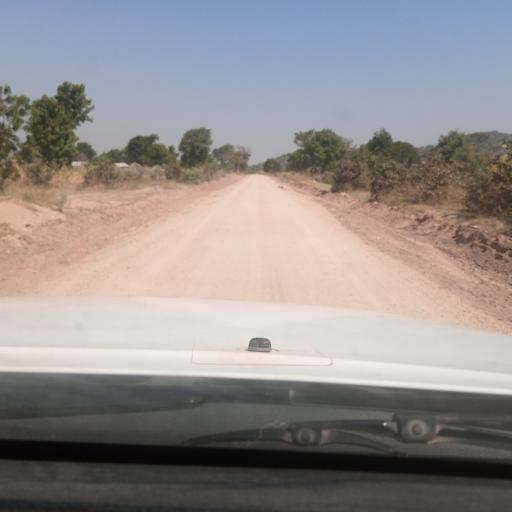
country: NG
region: Adamawa
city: Yola
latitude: 9.0603
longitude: 12.3867
